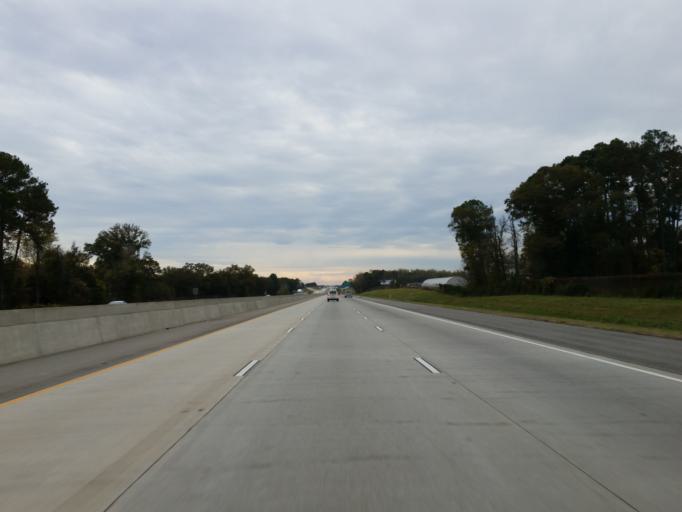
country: US
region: Georgia
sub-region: Cook County
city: Sparks
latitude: 31.2852
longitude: -83.4760
